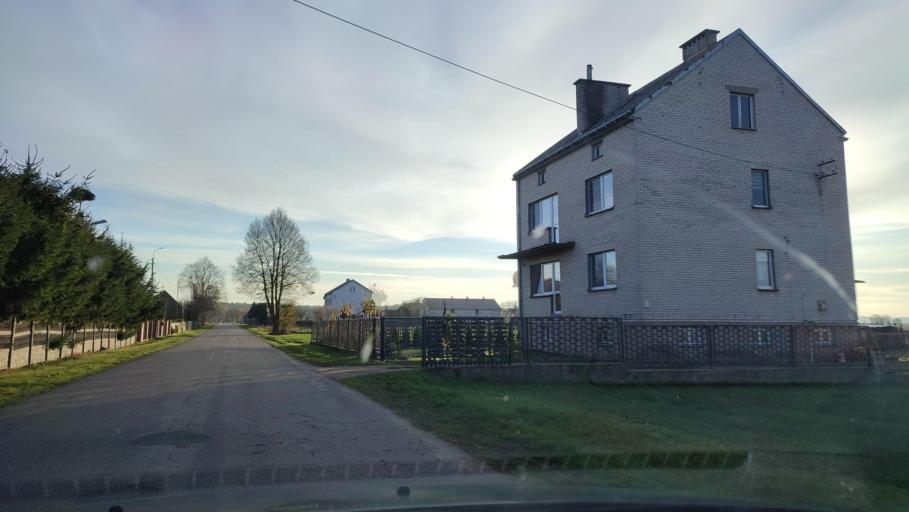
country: PL
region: Masovian Voivodeship
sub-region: Powiat mlawski
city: Dzierzgowo
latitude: 53.3106
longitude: 20.6712
